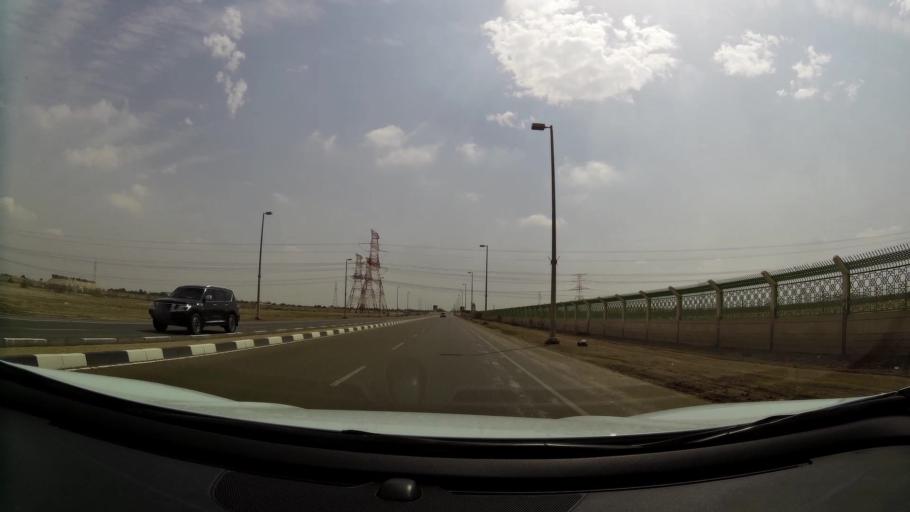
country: AE
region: Abu Dhabi
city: Abu Dhabi
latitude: 24.5266
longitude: 54.6436
